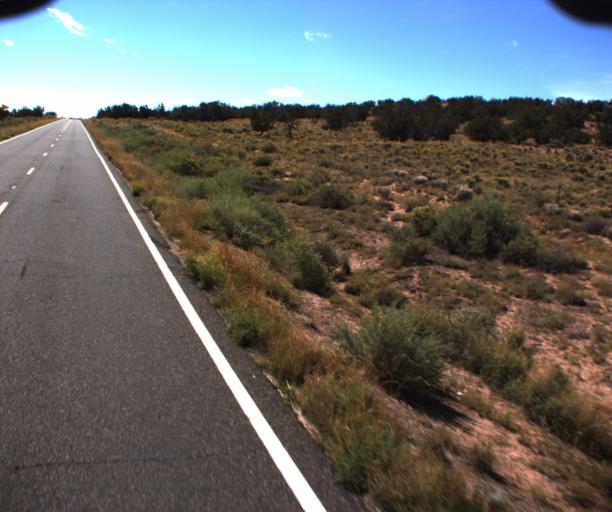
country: US
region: Arizona
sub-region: Apache County
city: Saint Johns
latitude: 34.7394
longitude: -109.2501
